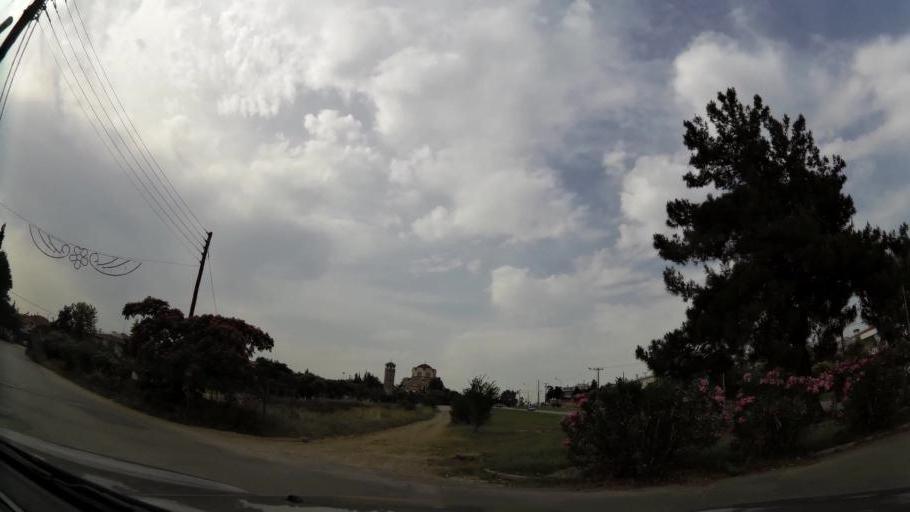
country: GR
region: Central Macedonia
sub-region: Nomos Thessalonikis
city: Oraiokastro
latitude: 40.7105
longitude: 22.9294
